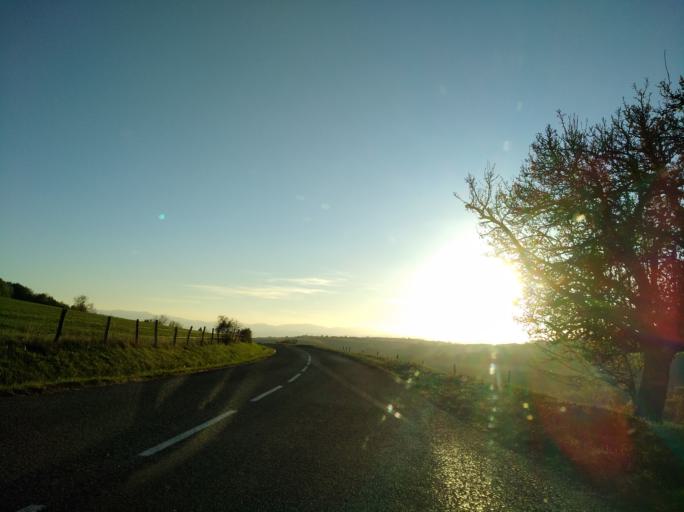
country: FR
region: Rhone-Alpes
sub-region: Departement du Rhone
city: Cogny
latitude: 45.9780
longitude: 4.5828
